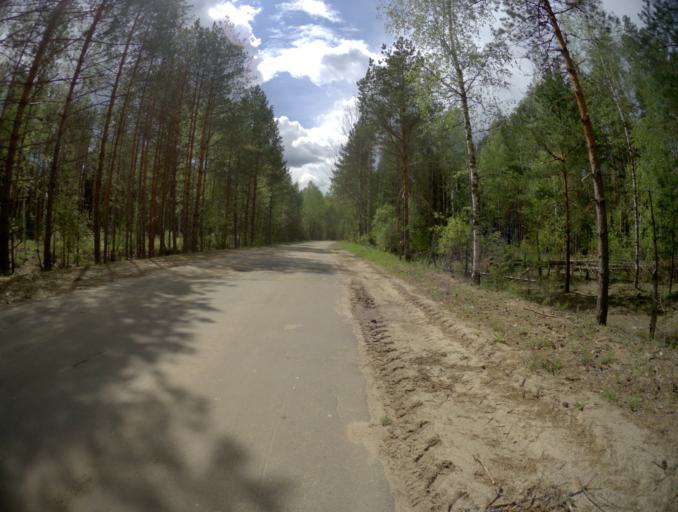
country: RU
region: Vladimir
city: Velikodvorskiy
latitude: 55.2479
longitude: 40.7613
